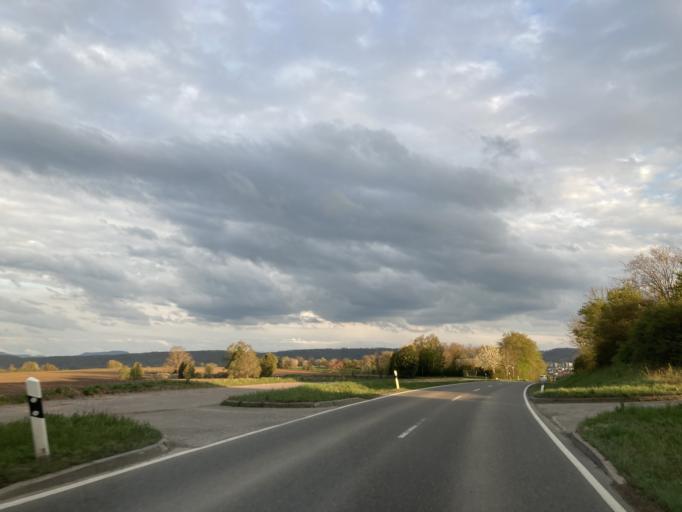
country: DE
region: Baden-Wuerttemberg
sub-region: Tuebingen Region
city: Rottenburg
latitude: 48.4948
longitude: 8.9360
